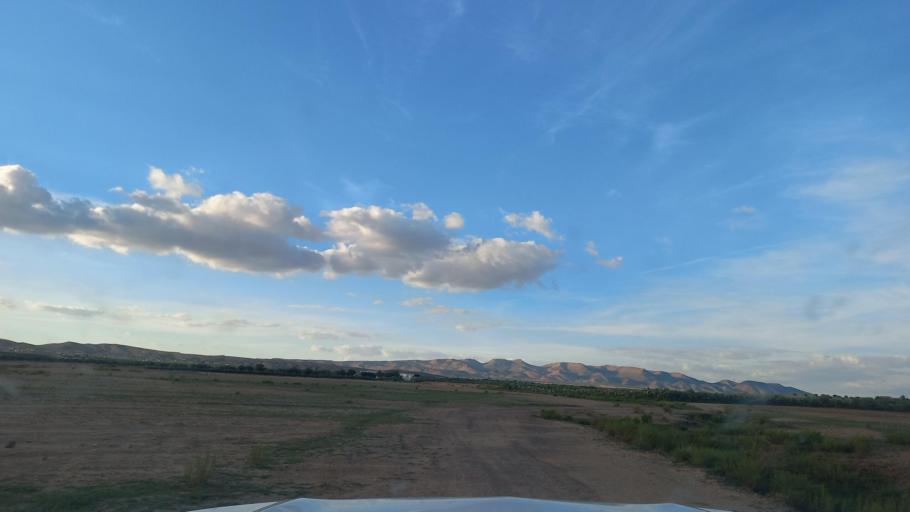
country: TN
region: Al Qasrayn
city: Sbiba
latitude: 35.3527
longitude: 9.0318
